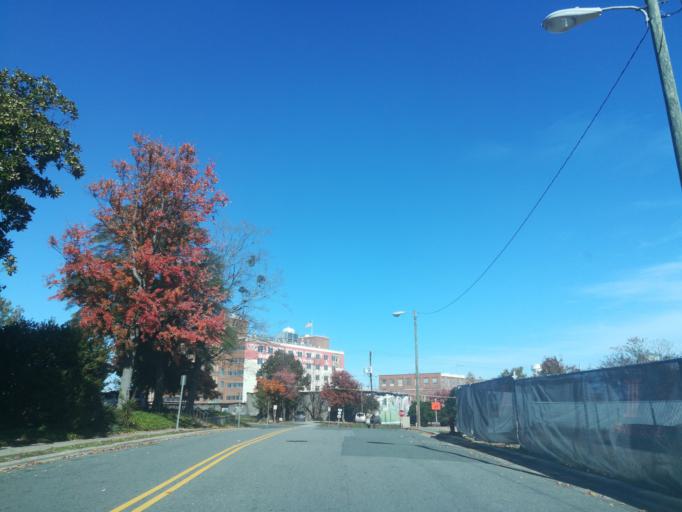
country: US
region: North Carolina
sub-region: Durham County
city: Durham
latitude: 35.9963
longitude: -78.9075
